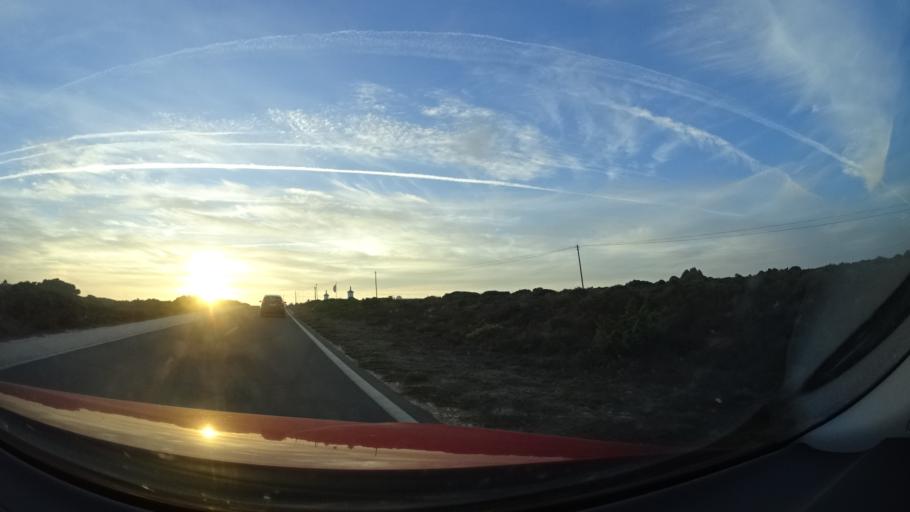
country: PT
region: Faro
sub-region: Vila do Bispo
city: Sagres
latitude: 37.0274
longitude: -8.9774
